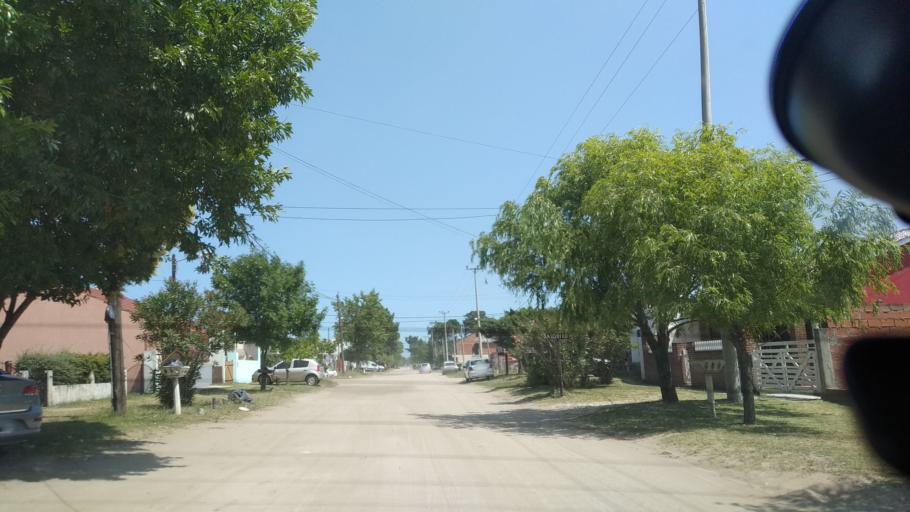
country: AR
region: Buenos Aires
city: Mar del Tuyu
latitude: -36.5819
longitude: -56.6935
